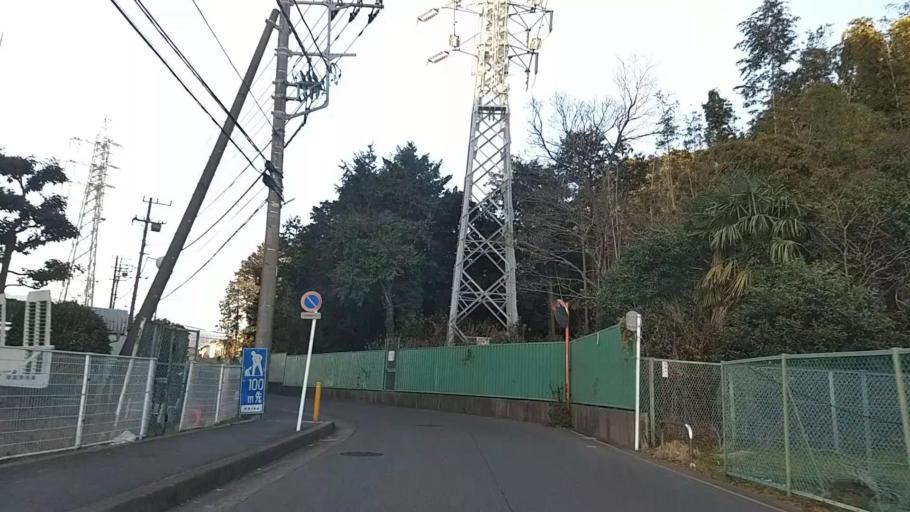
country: JP
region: Kanagawa
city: Atsugi
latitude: 35.4542
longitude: 139.3341
